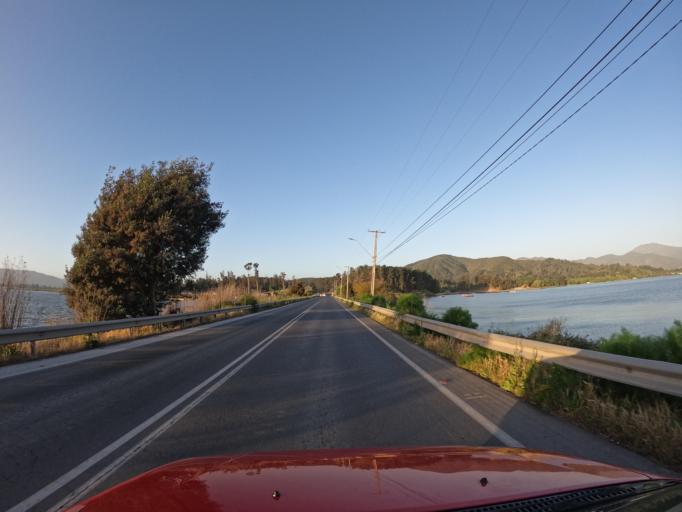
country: CL
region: O'Higgins
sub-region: Provincia de Cachapoal
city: San Vicente
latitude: -34.1481
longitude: -71.3821
